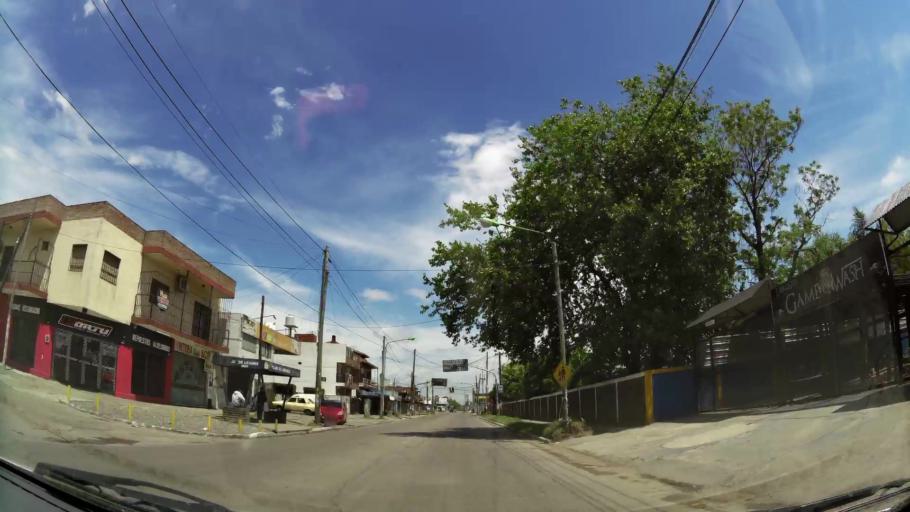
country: AR
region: Buenos Aires
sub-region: Partido de Quilmes
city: Quilmes
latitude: -34.7885
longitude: -58.2768
